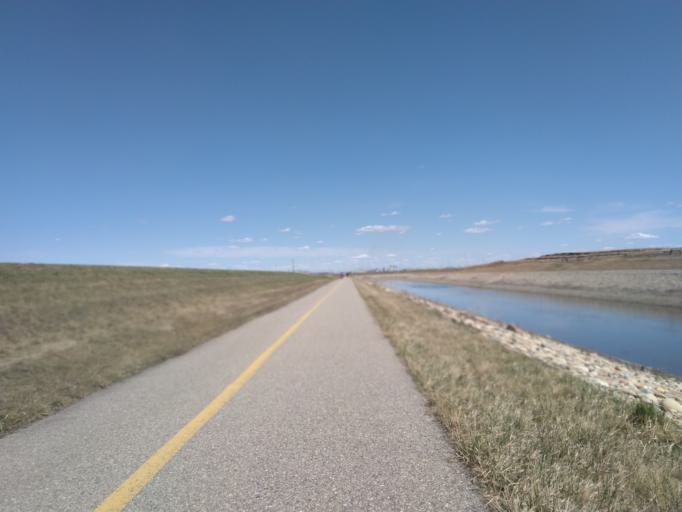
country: CA
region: Alberta
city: Chestermere
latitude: 50.9723
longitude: -113.9301
